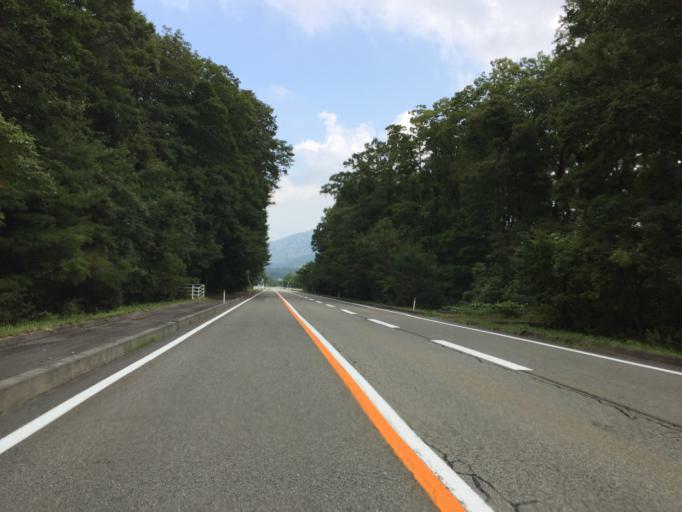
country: JP
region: Fukushima
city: Funehikimachi-funehiki
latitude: 37.5762
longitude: 140.7268
